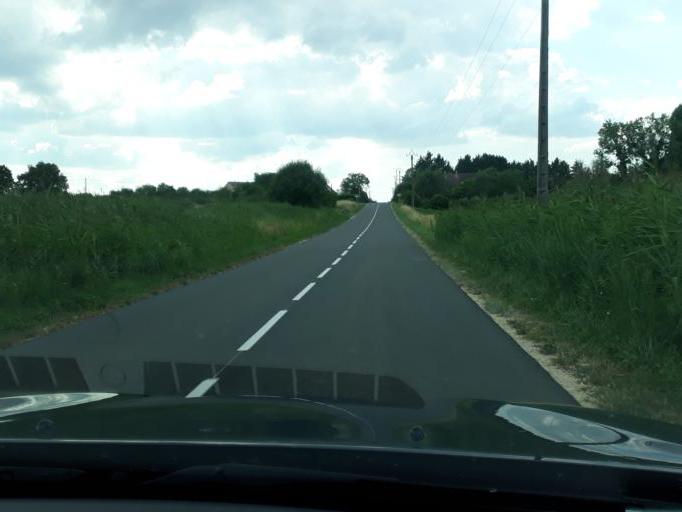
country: FR
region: Centre
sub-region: Departement du Cher
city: Baugy
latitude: 47.0805
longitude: 2.7464
